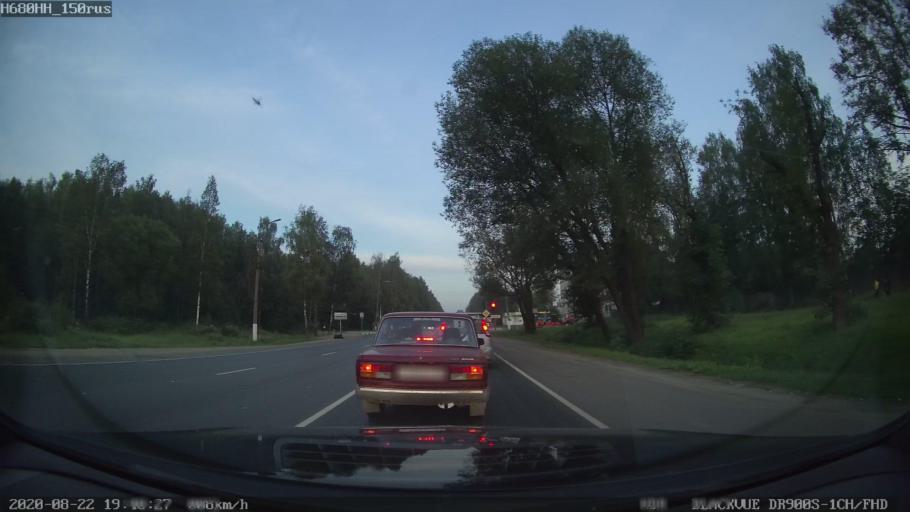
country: RU
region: Tverskaya
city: Emmaus
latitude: 56.8044
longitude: 36.0250
